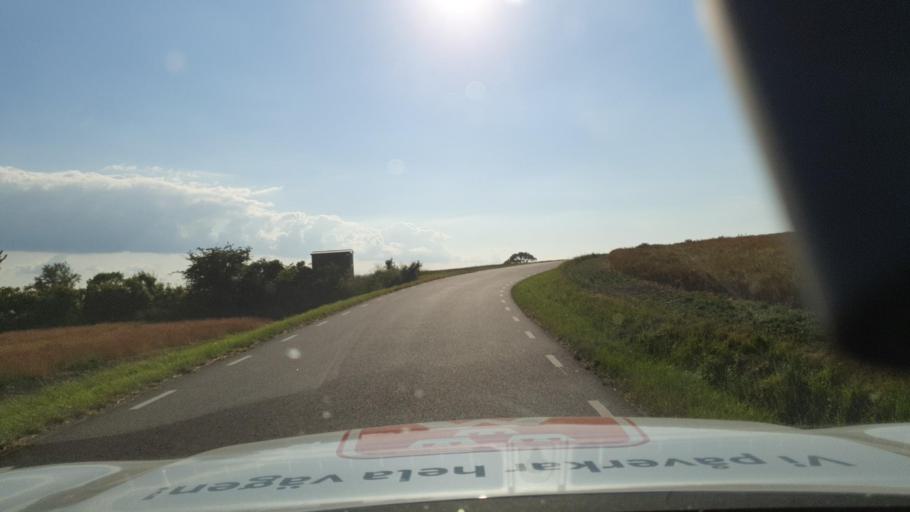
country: SE
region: Skane
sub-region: Skurups Kommun
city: Rydsgard
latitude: 55.5061
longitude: 13.5608
